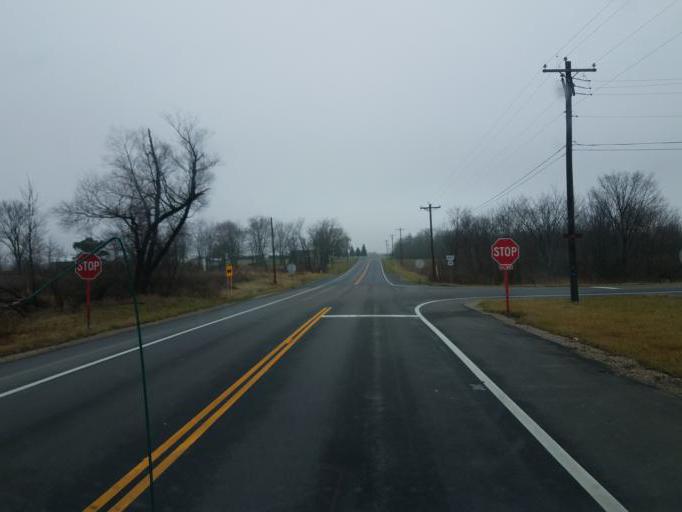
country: US
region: Ohio
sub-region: Champaign County
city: North Lewisburg
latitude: 40.2737
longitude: -83.5397
